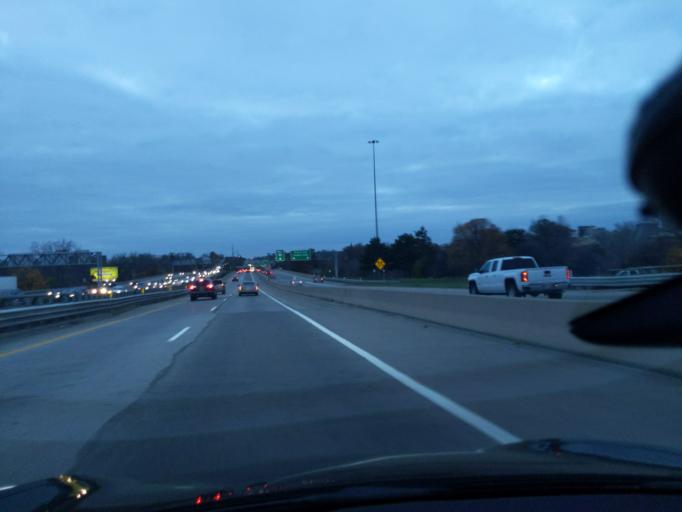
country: US
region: Michigan
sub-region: Ingham County
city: Lansing
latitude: 42.7257
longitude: -84.5426
